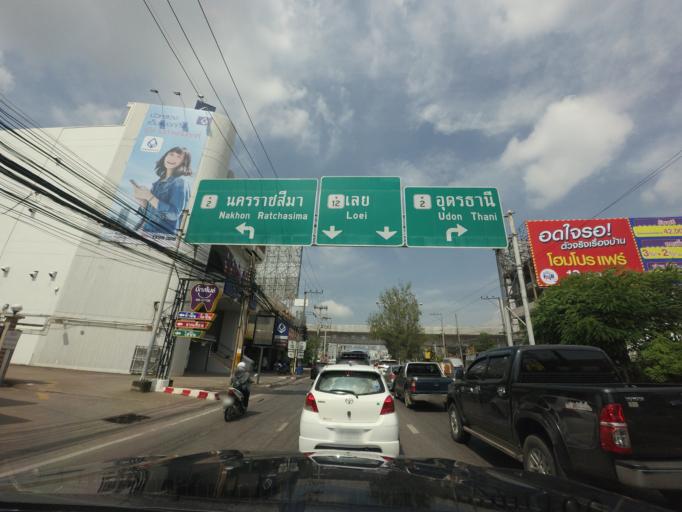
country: TH
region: Khon Kaen
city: Khon Kaen
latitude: 16.4394
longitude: 102.8301
